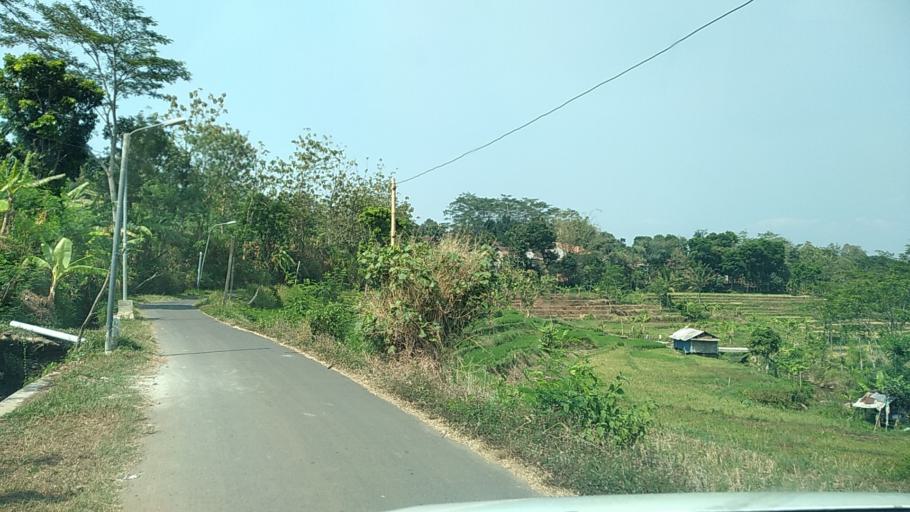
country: ID
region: Central Java
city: Ungaran
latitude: -7.0876
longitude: 110.3392
